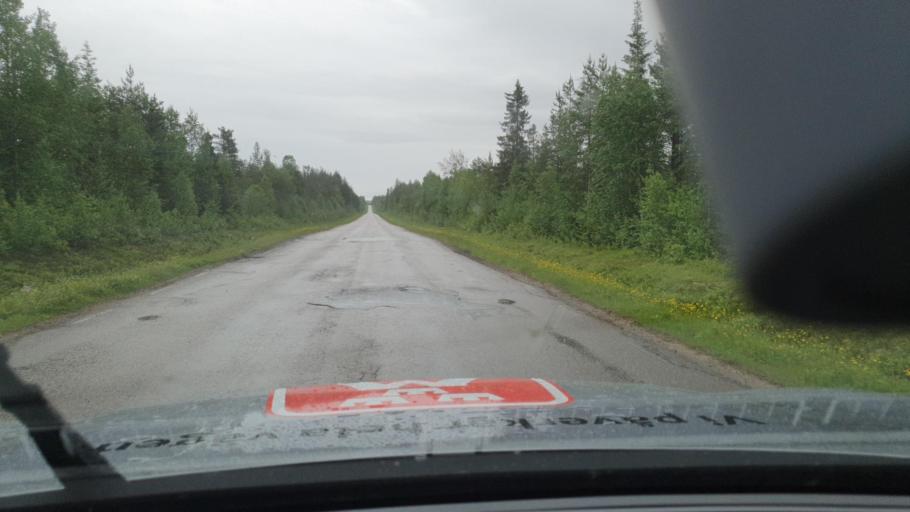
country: SE
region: Norrbotten
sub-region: Pajala Kommun
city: Pajala
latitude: 66.8382
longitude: 23.0876
